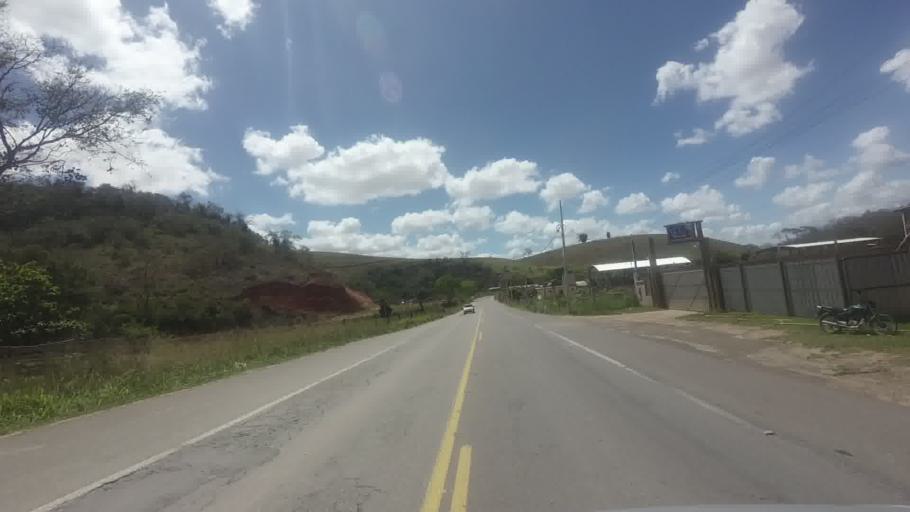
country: BR
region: Rio de Janeiro
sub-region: Santo Antonio De Padua
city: Santo Antonio de Padua
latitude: -21.6566
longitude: -42.3282
